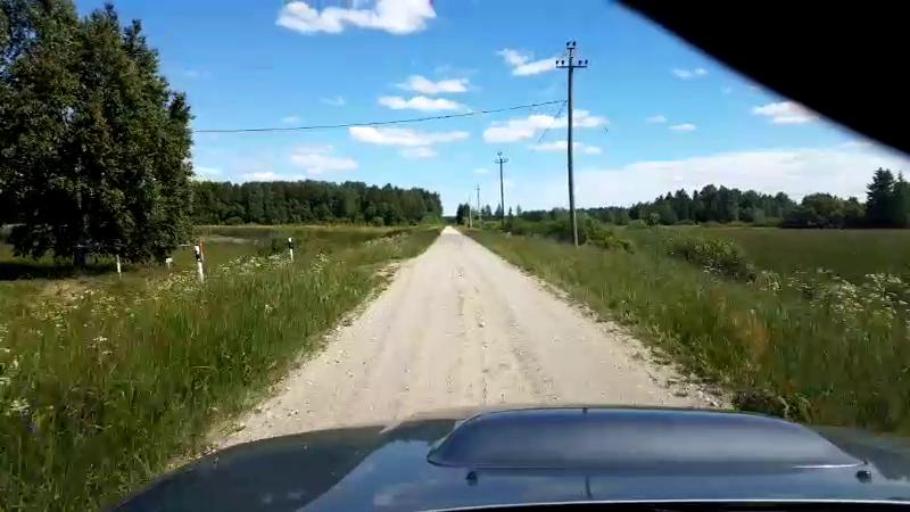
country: EE
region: Paernumaa
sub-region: Halinga vald
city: Parnu-Jaagupi
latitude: 58.5319
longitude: 24.5358
